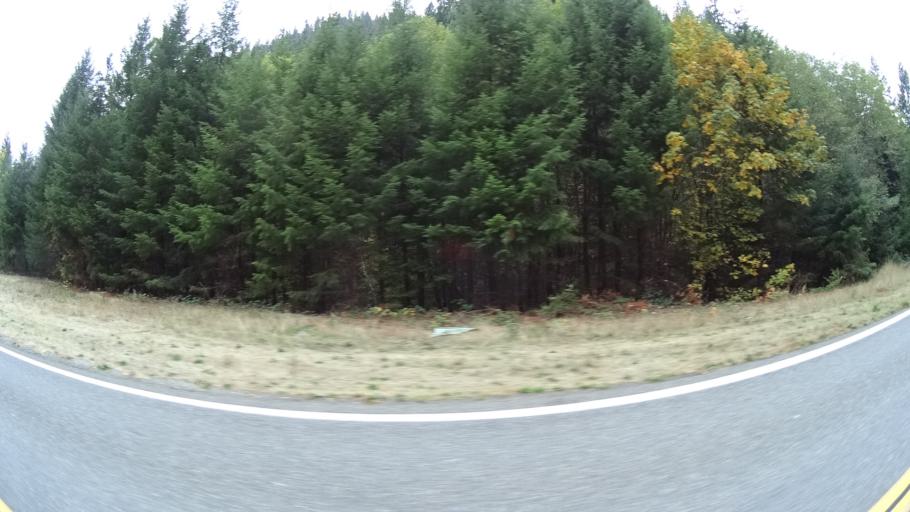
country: US
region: California
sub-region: Siskiyou County
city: Happy Camp
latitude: 41.9078
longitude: -123.4433
